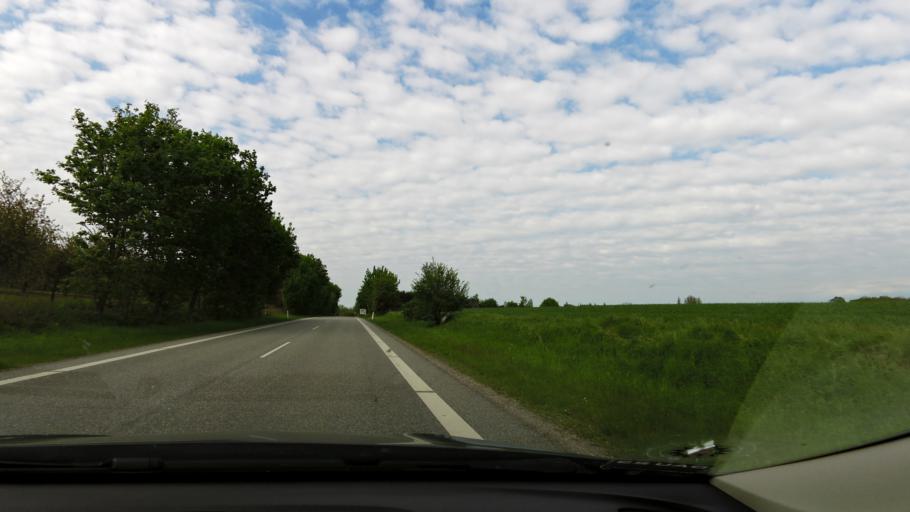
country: DK
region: South Denmark
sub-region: Nyborg Kommune
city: Nyborg
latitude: 55.3101
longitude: 10.7277
